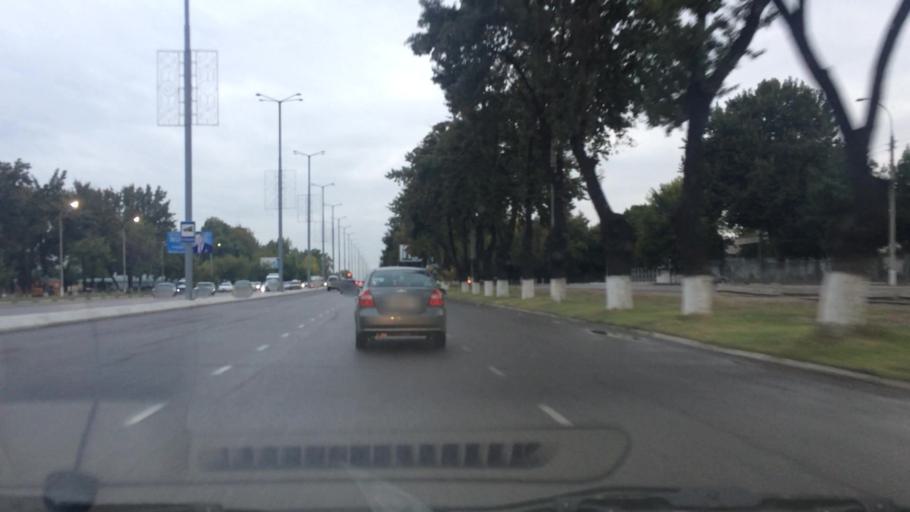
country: UZ
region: Toshkent Shahri
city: Tashkent
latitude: 41.2545
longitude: 69.1898
